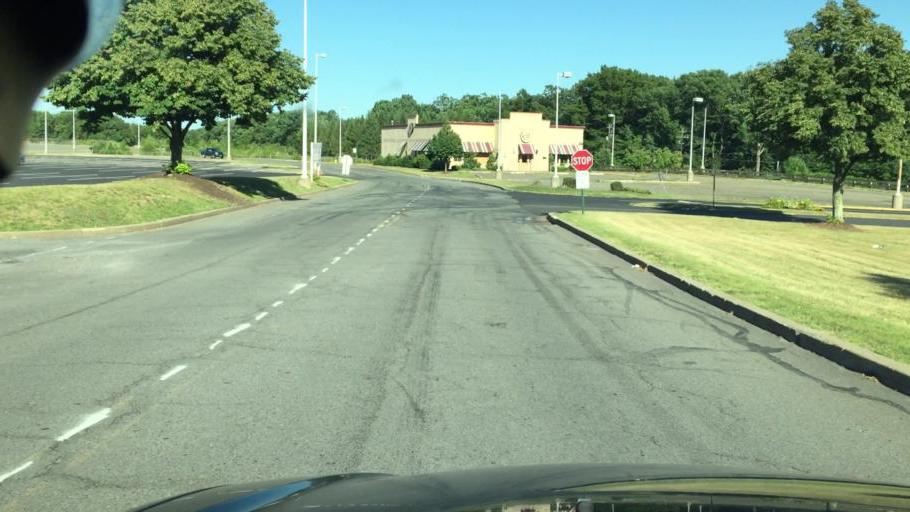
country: US
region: Pennsylvania
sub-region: Luzerne County
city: West Hazleton
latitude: 40.9827
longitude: -76.0164
